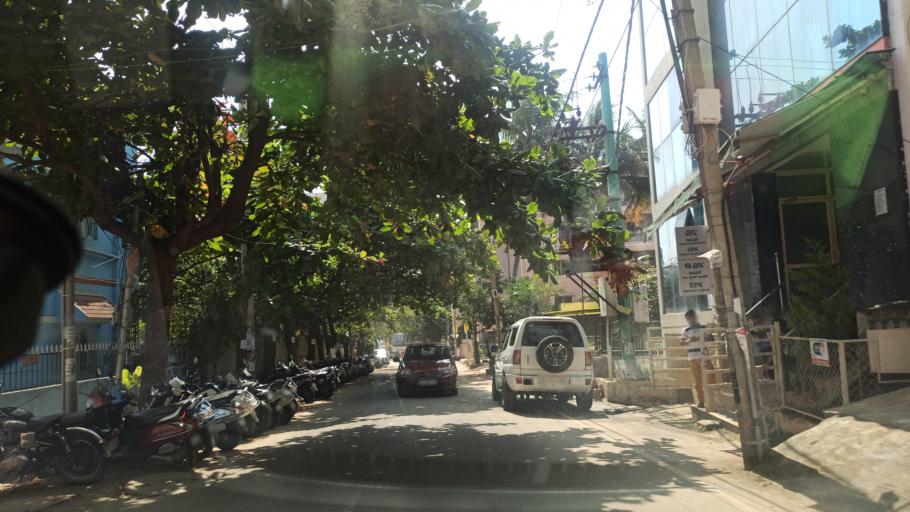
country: IN
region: Karnataka
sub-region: Bangalore Urban
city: Yelahanka
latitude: 13.0520
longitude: 77.5977
